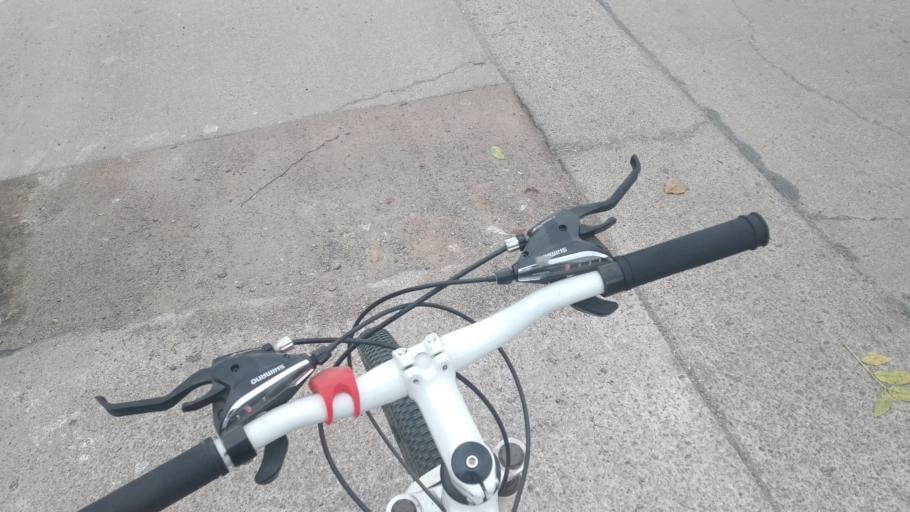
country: AR
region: Cordoba
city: Leones
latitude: -32.6623
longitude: -62.3027
